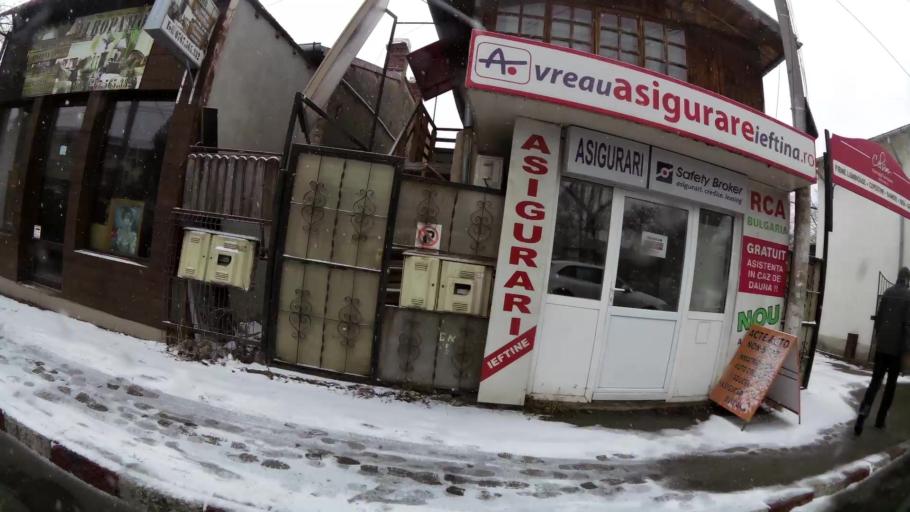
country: RO
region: Dambovita
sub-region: Municipiul Targoviste
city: Targoviste
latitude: 44.9190
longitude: 25.4640
